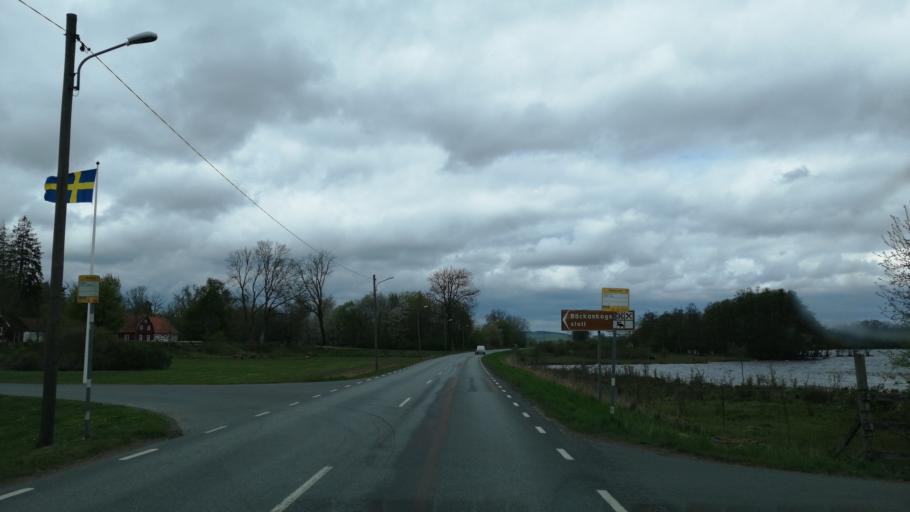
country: SE
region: Skane
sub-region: Kristianstads Kommun
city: Fjalkinge
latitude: 56.0855
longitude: 14.3503
